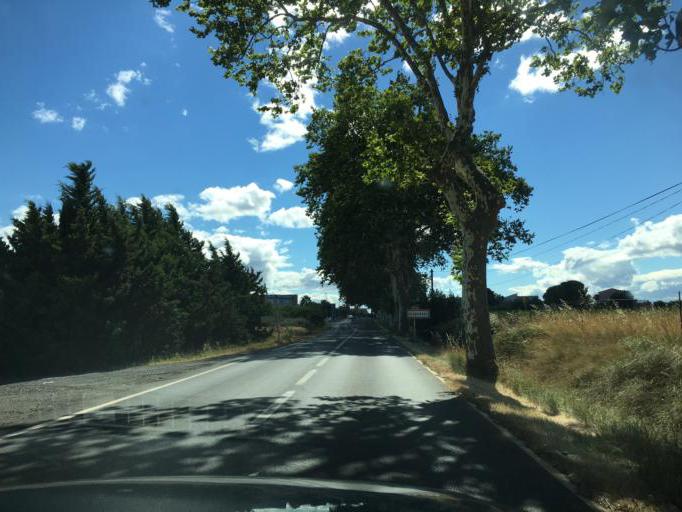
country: FR
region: Languedoc-Roussillon
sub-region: Departement de l'Herault
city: Florensac
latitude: 43.3869
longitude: 3.4806
